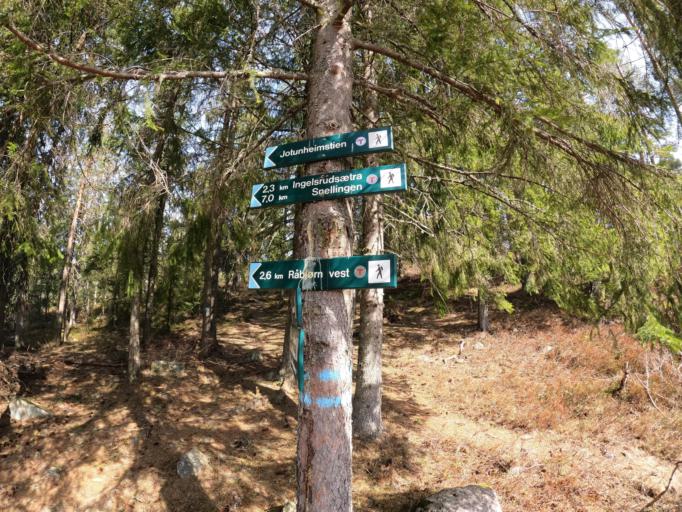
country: NO
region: Akershus
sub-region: Nittedal
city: Aneby
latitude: 60.2363
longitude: 10.8551
